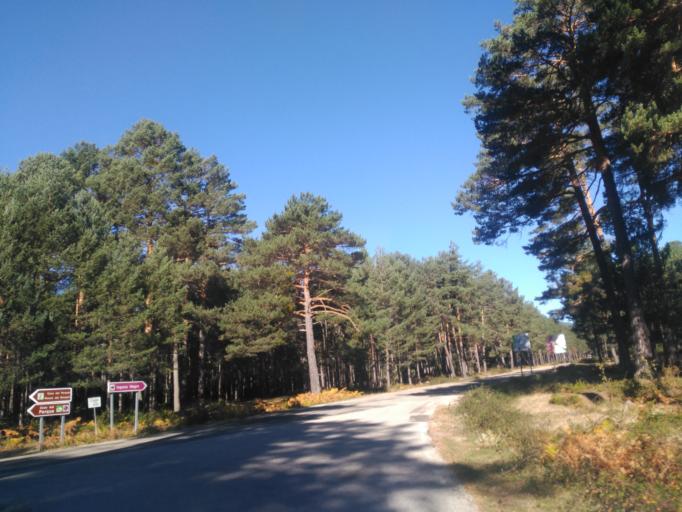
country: ES
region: Castille and Leon
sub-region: Provincia de Soria
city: Vinuesa
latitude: 41.9789
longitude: -2.7946
